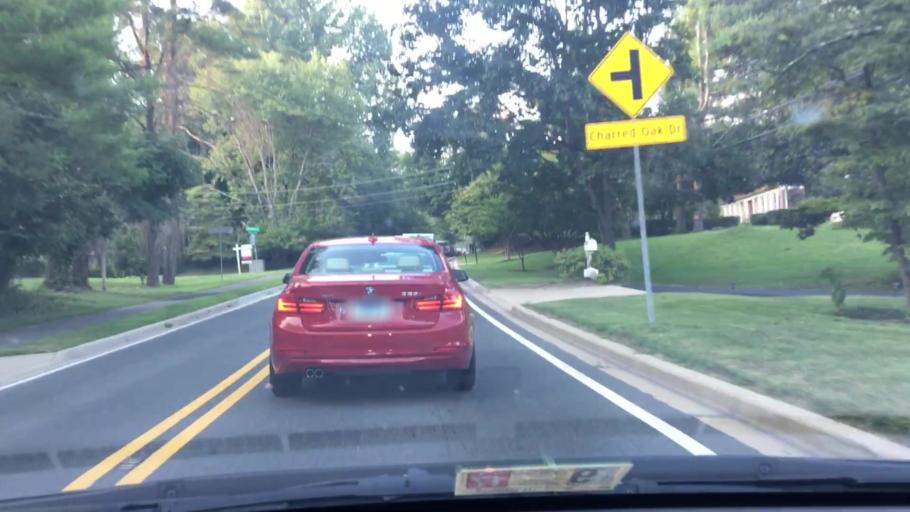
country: US
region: Maryland
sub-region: Montgomery County
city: Cabin John
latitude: 39.0024
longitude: -77.1598
